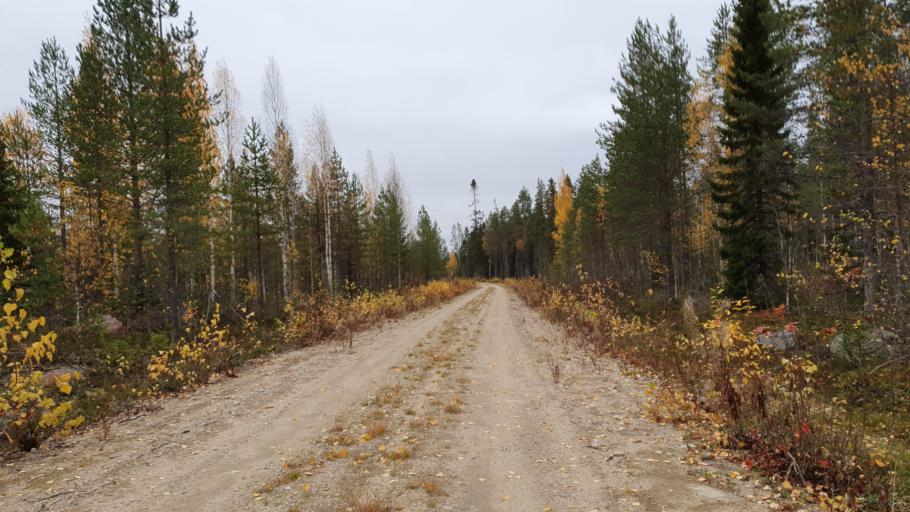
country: FI
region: Kainuu
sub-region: Kehys-Kainuu
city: Kuhmo
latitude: 64.4416
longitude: 29.6172
